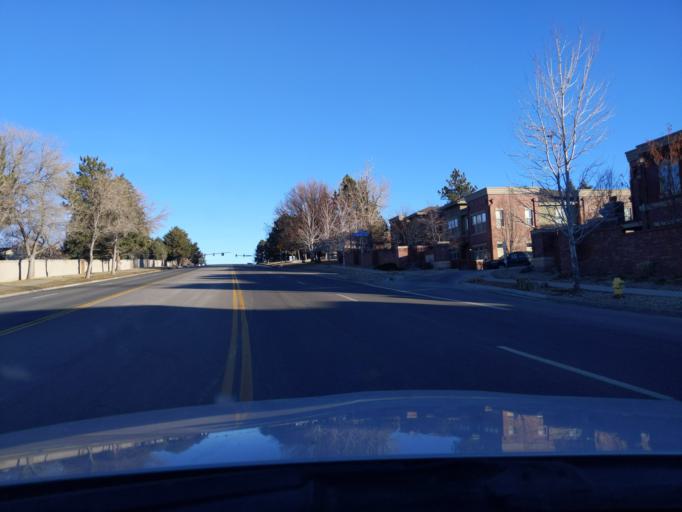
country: US
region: Colorado
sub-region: Arapahoe County
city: Centennial
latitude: 39.5699
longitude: -104.8857
